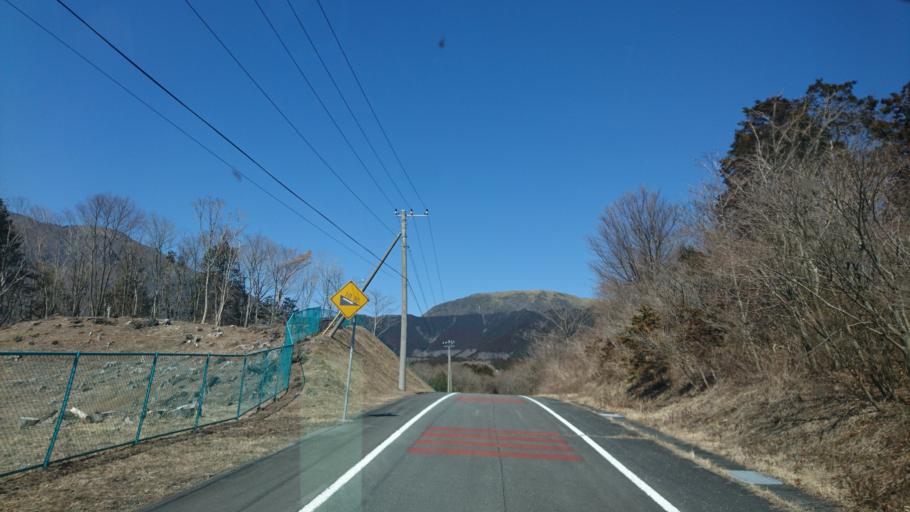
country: JP
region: Yamanashi
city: Fujikawaguchiko
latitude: 35.4161
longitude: 138.5969
